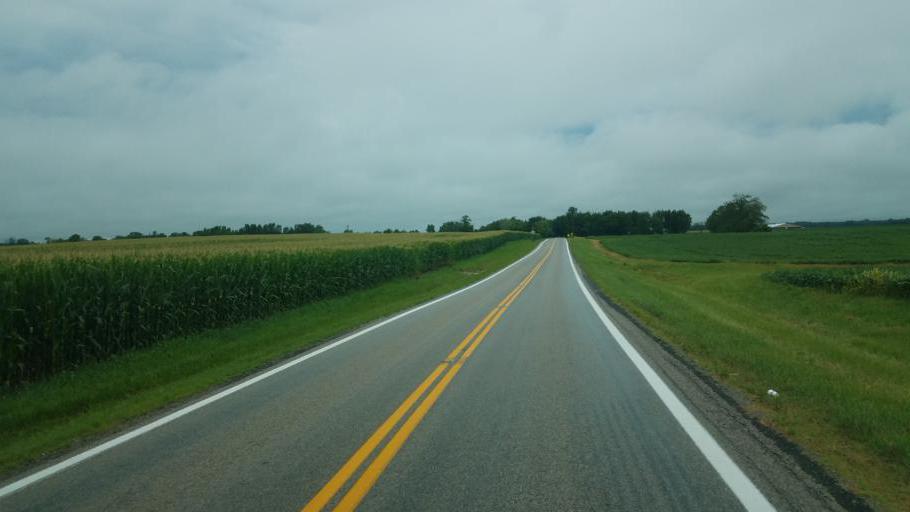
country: US
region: Ohio
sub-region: Union County
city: Richwood
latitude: 40.5368
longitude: -83.3565
